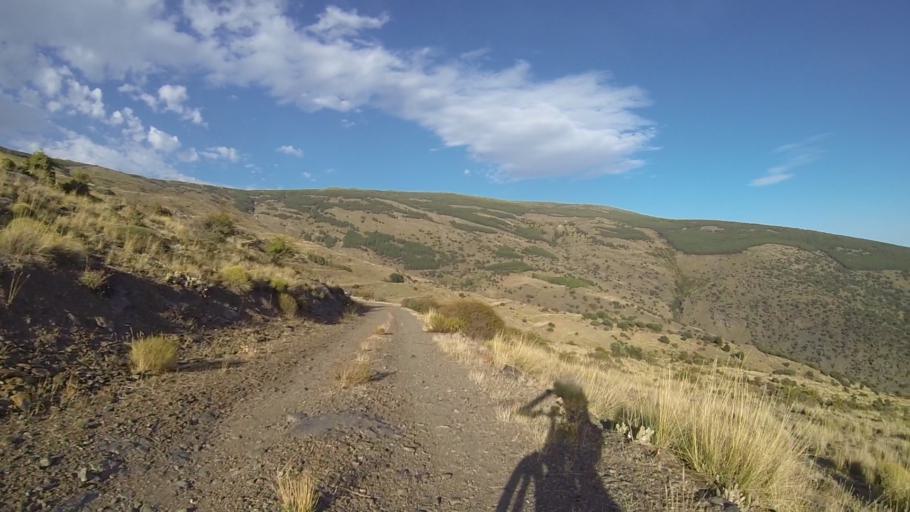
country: ES
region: Andalusia
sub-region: Provincia de Almeria
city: Laujar de Andarax
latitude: 37.0657
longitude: -2.8859
